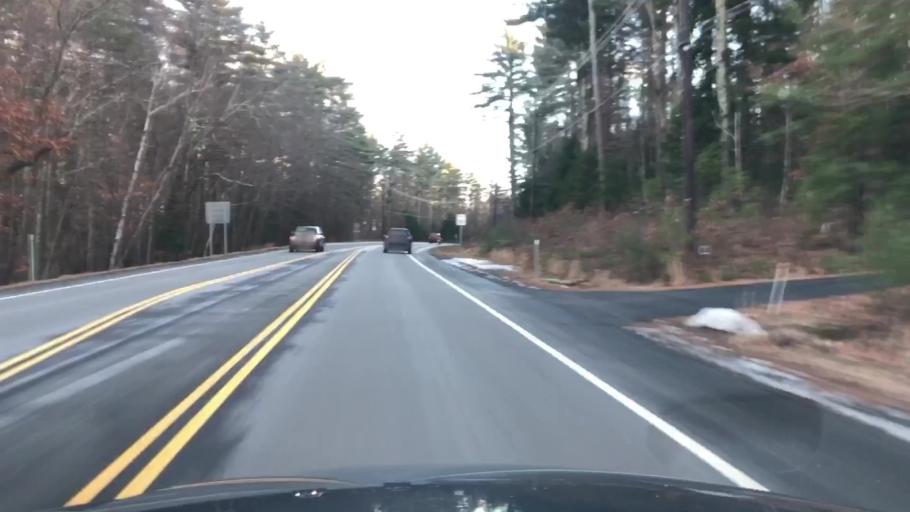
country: US
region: New Hampshire
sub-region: Hillsborough County
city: Brookline
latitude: 42.7480
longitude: -71.6682
